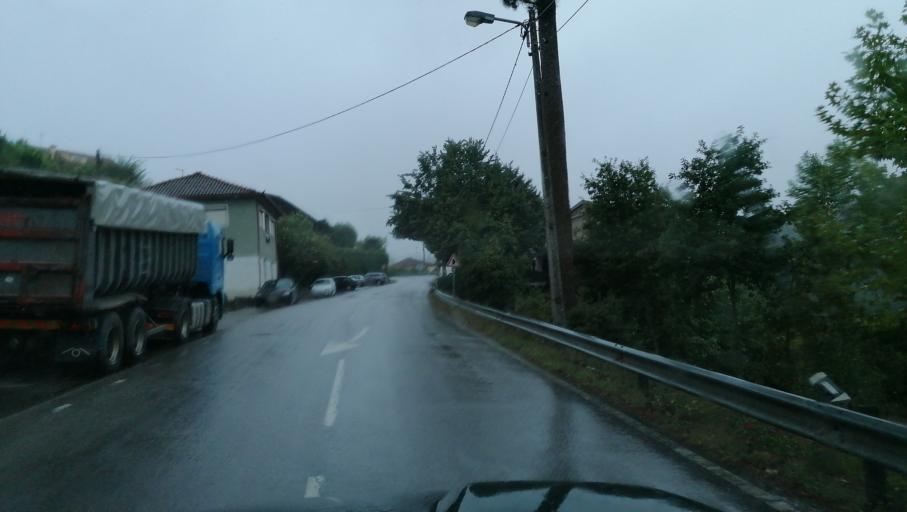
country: PT
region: Braga
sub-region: Cabeceiras de Basto
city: Cabeceiras de Basto
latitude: 41.4903
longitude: -7.9610
